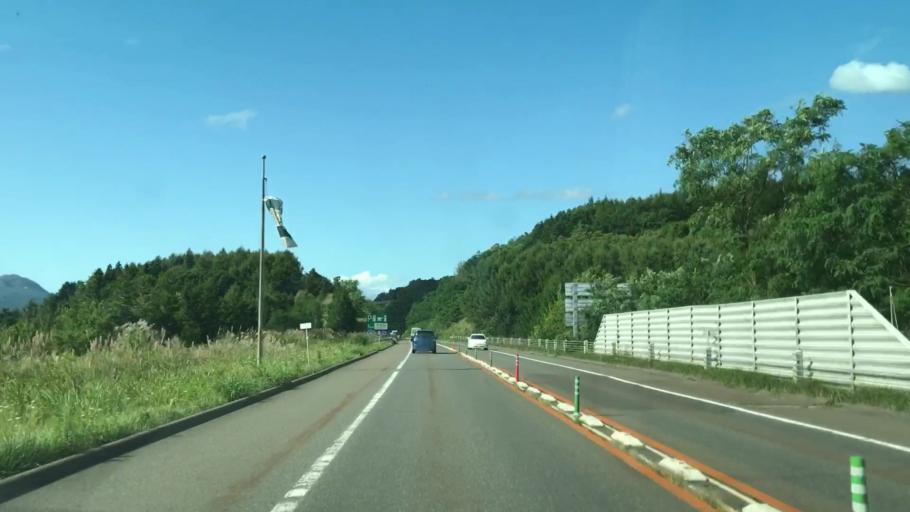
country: JP
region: Hokkaido
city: Date
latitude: 42.4537
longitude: 140.9130
